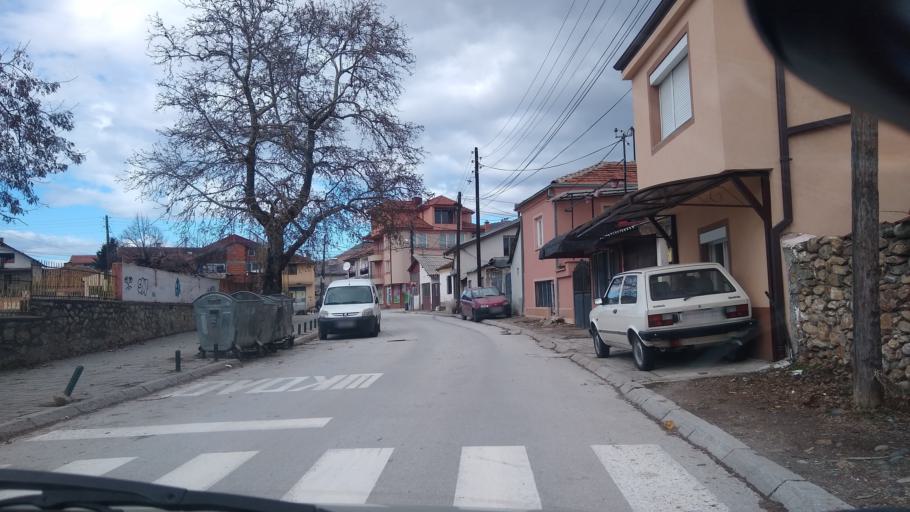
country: MK
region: Bitola
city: Bitola
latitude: 41.0278
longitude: 21.3268
